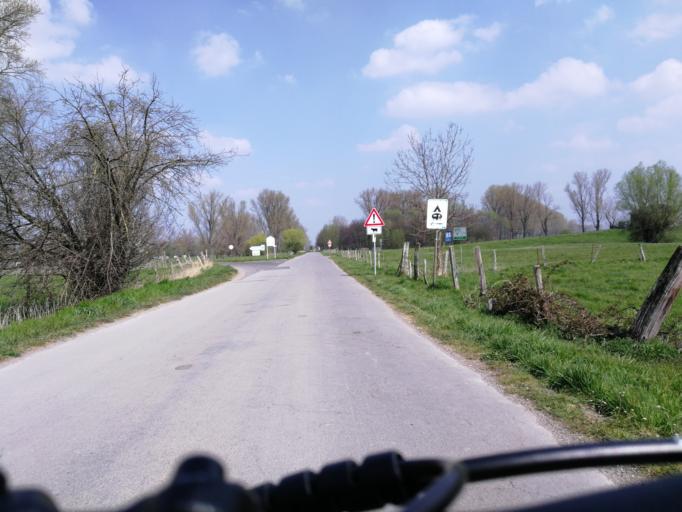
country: DE
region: North Rhine-Westphalia
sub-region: Regierungsbezirk Dusseldorf
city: Dormagen
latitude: 51.1418
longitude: 6.8219
